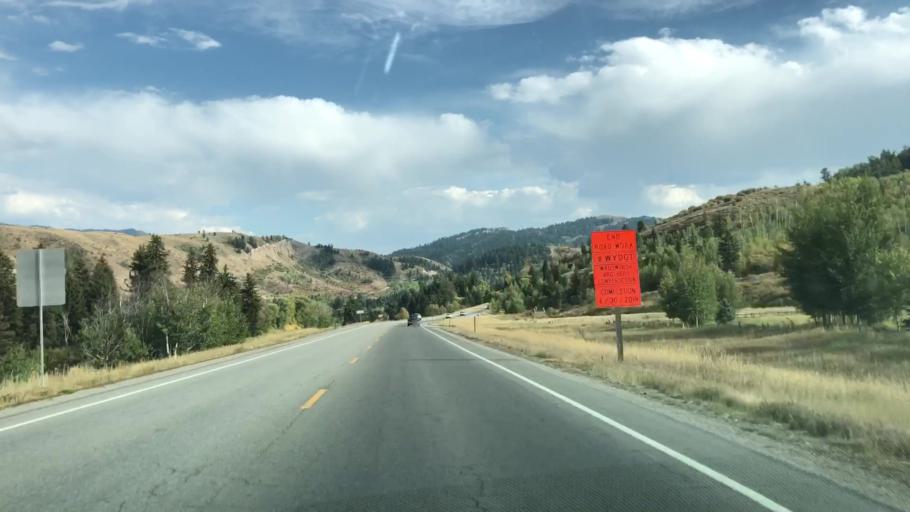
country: US
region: Wyoming
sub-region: Teton County
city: South Park
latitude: 43.3640
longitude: -110.7302
